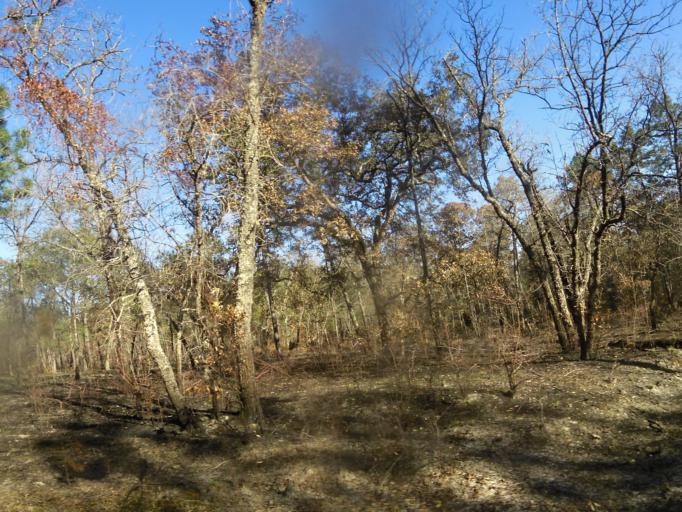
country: US
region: Florida
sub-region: Clay County
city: Middleburg
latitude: 30.1357
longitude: -81.9045
